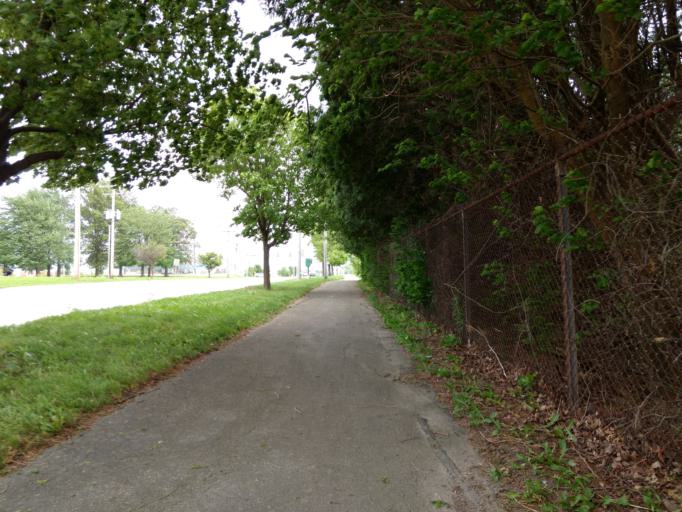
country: US
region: Illinois
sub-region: Champaign County
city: Urbana
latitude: 40.0837
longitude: -88.1926
